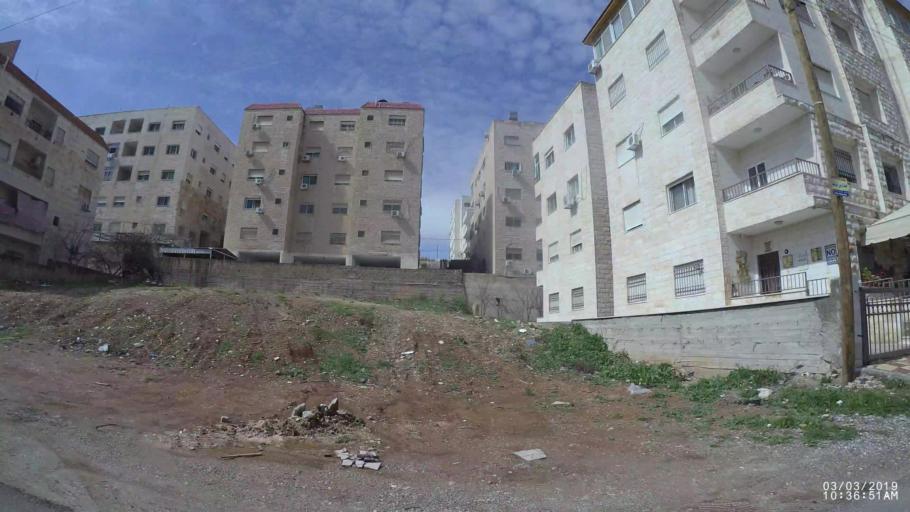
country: JO
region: Amman
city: Al Jubayhah
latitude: 31.9948
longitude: 35.9075
